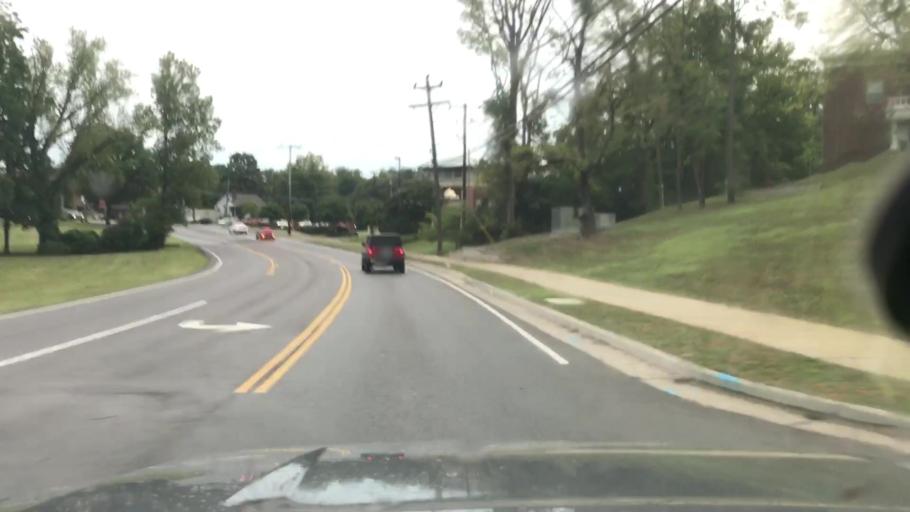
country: US
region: Tennessee
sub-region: Davidson County
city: Lakewood
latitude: 36.1758
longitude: -86.6156
